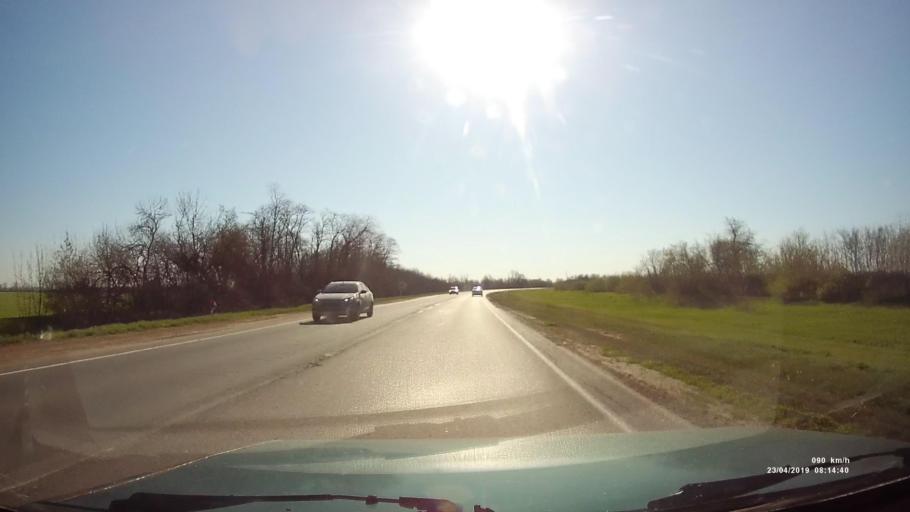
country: RU
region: Rostov
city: Yegorlykskaya
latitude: 46.5463
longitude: 40.7616
